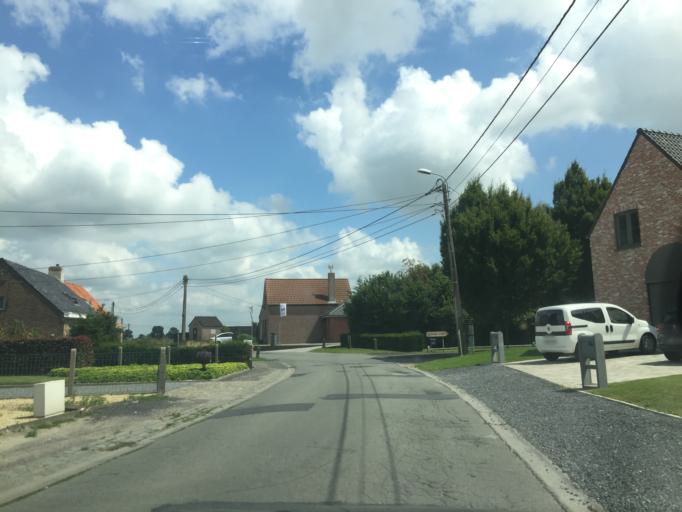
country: BE
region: Flanders
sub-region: Provincie West-Vlaanderen
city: Kortemark
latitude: 51.0375
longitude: 3.0415
